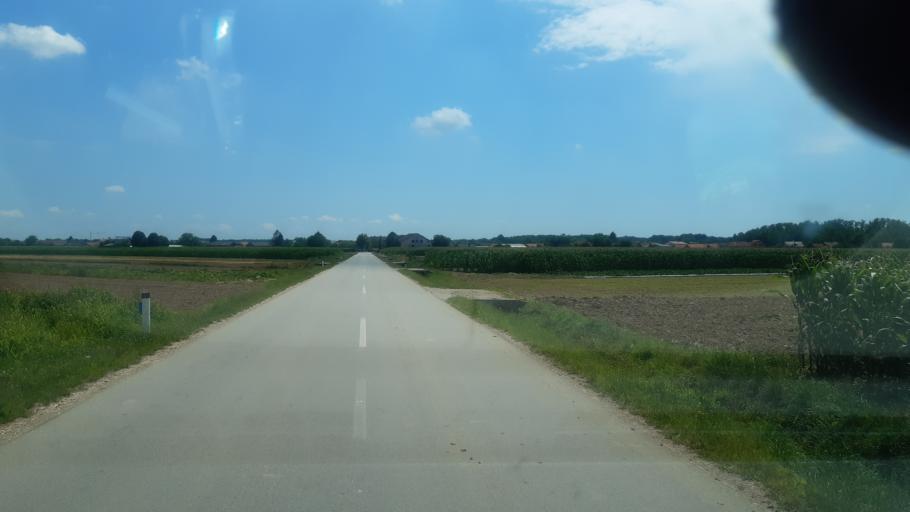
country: SI
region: Moravske Toplice
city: Moravske Toplice
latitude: 46.6744
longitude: 16.2028
